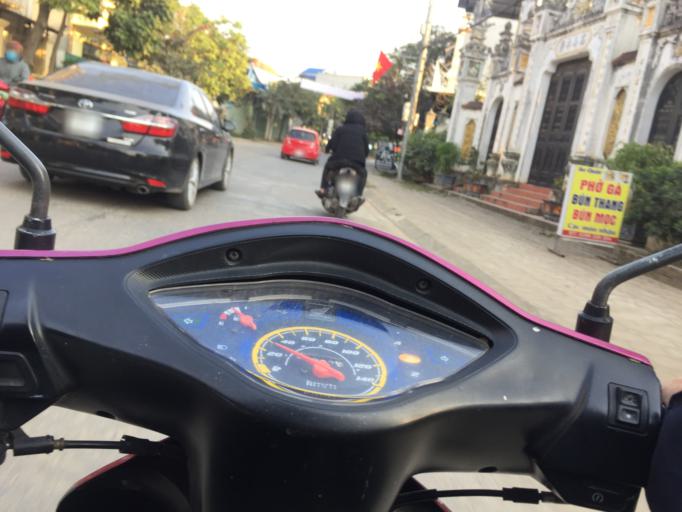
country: VN
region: Ha Noi
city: Chuc Son
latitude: 20.9206
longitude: 105.7120
